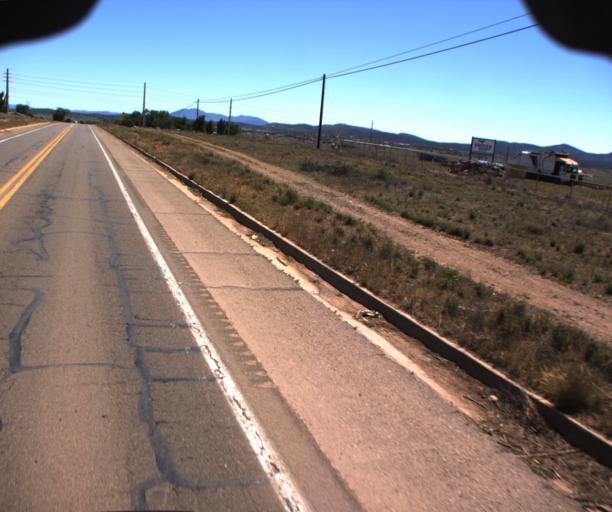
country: US
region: Arizona
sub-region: Yavapai County
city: Paulden
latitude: 34.8902
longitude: -112.4674
